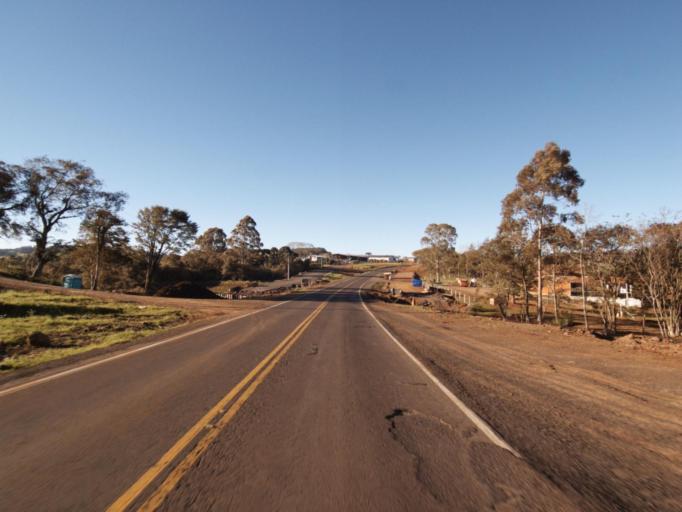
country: AR
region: Misiones
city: Bernardo de Irigoyen
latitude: -26.4274
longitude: -53.5210
